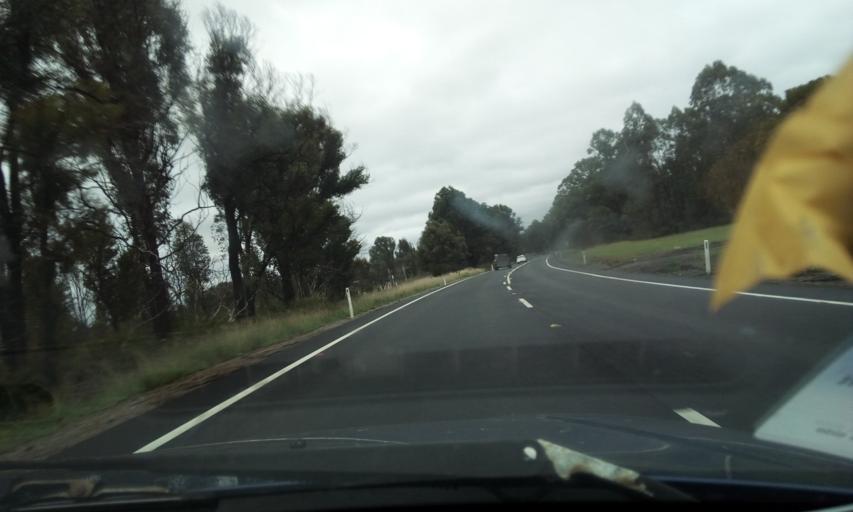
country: AU
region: New South Wales
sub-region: Penrith Municipality
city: Werrington Downs
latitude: -33.7032
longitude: 150.7244
